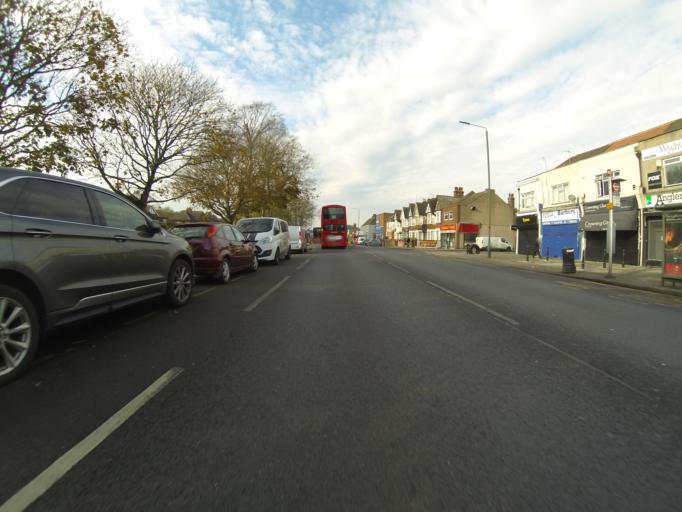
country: GB
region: England
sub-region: Greater London
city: Welling
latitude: 51.4602
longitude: 0.1216
